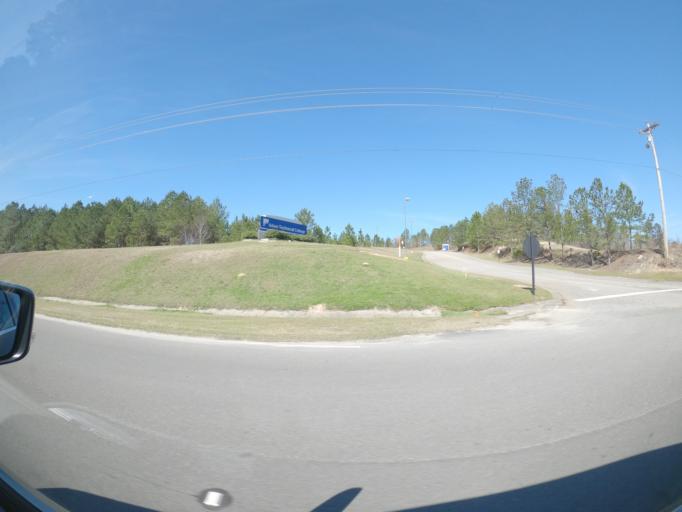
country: US
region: South Carolina
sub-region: Aiken County
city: Gloverville
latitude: 33.5340
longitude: -81.8383
